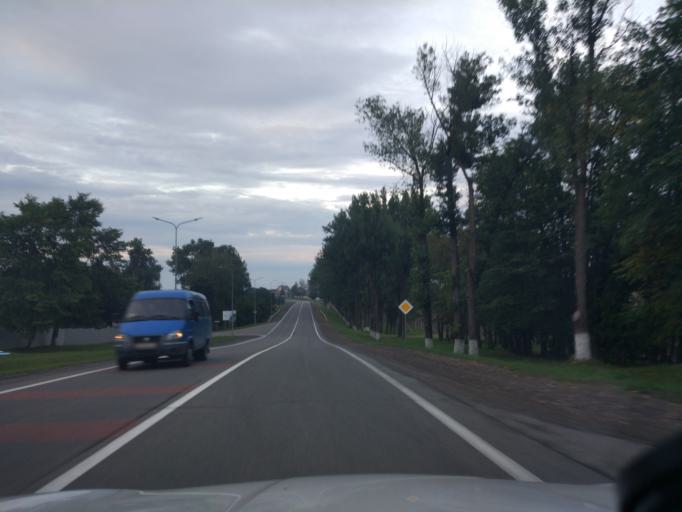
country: BY
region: Minsk
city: Astrashytski Haradok
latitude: 54.0607
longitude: 27.7005
